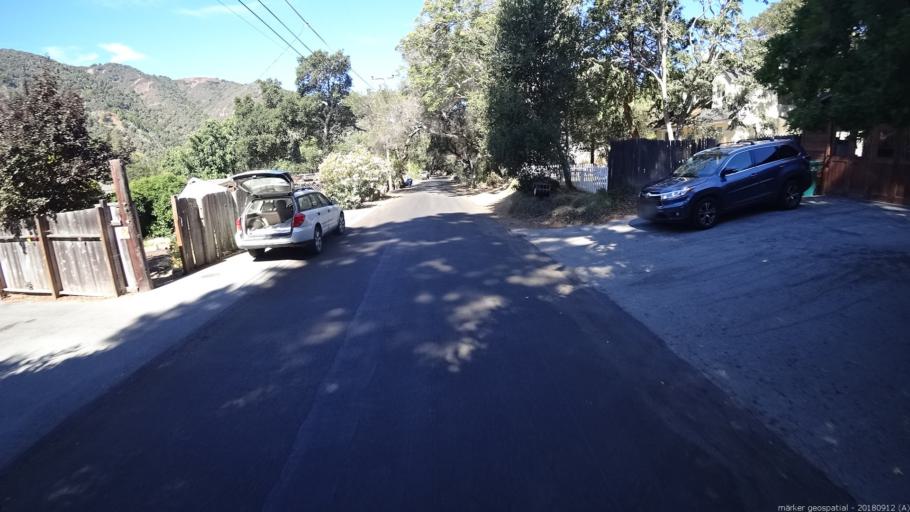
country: US
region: California
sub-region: Monterey County
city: Carmel Valley Village
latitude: 36.4781
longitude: -121.7355
